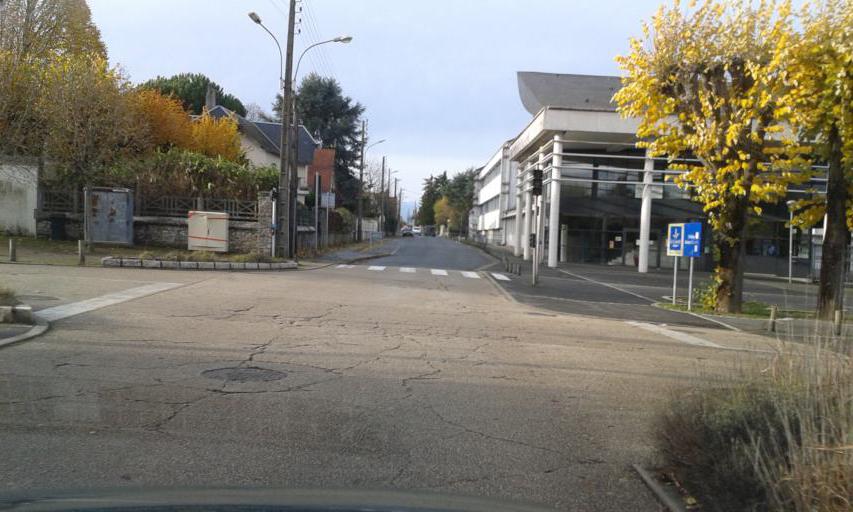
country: FR
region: Centre
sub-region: Departement du Loiret
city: Beaugency
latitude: 47.7746
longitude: 1.6286
